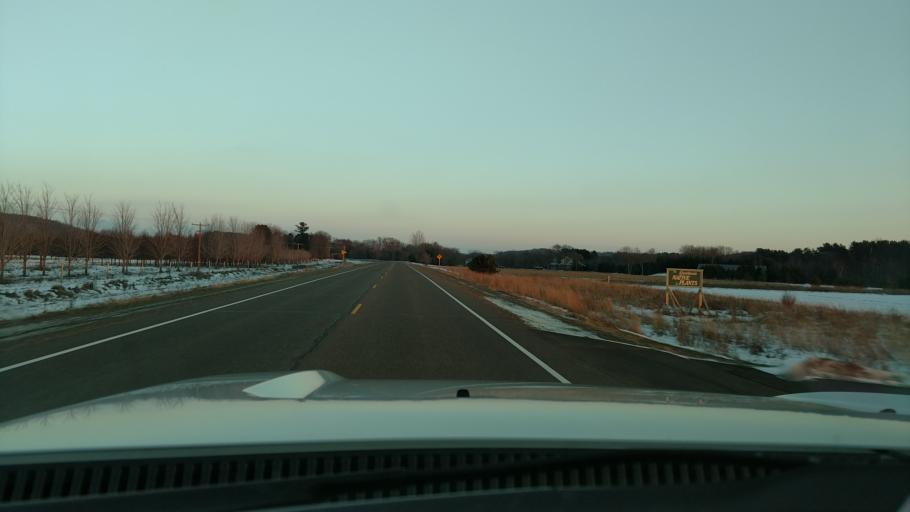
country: US
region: Wisconsin
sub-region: Pierce County
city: River Falls
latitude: 44.8983
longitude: -92.5939
